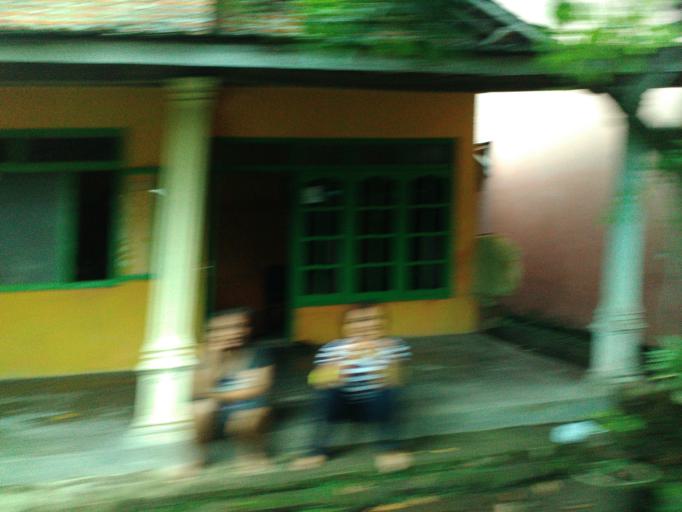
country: ID
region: Central Java
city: Delanggu
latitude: -7.6364
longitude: 110.6960
